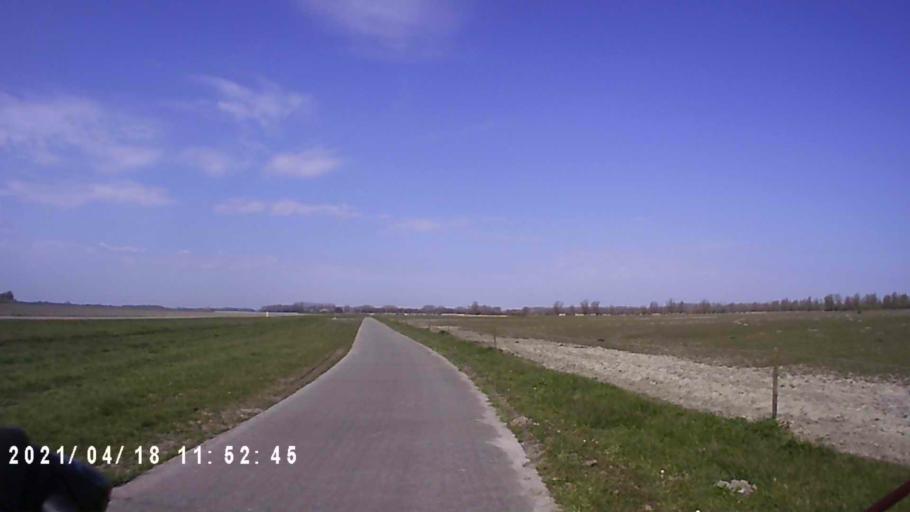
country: NL
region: Friesland
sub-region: Gemeente Kollumerland en Nieuwkruisland
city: Kollum
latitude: 53.3210
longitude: 6.2163
